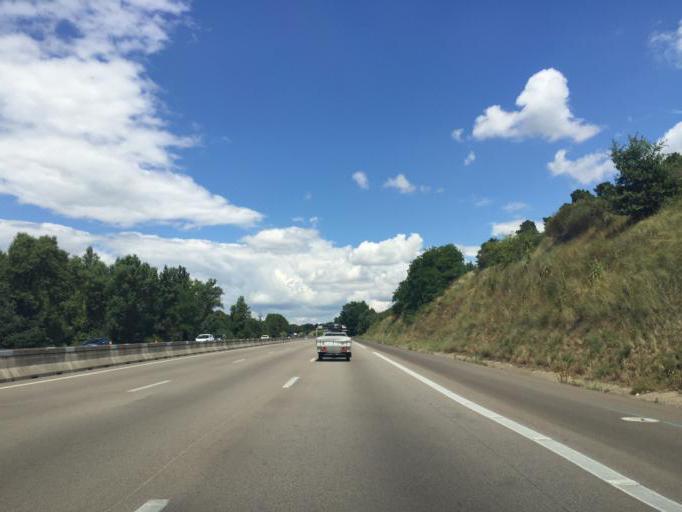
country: FR
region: Rhone-Alpes
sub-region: Departement de la Drome
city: Saint-Barthelemy-de-Vals
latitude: 45.1359
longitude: 4.8935
